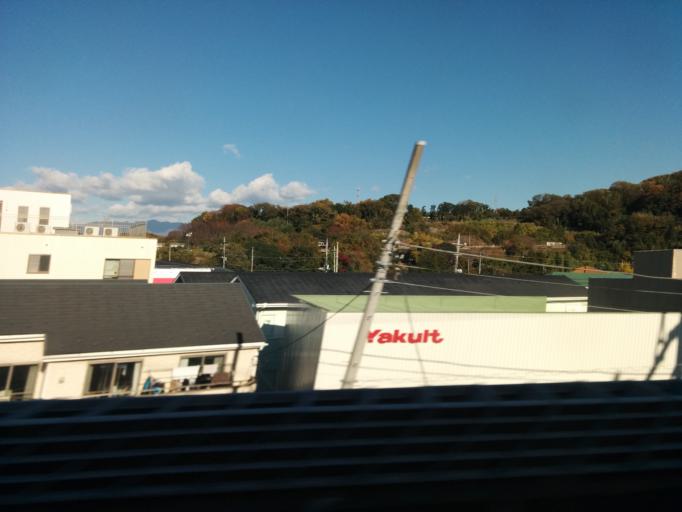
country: JP
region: Kanagawa
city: Ninomiya
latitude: 35.3084
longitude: 139.2521
